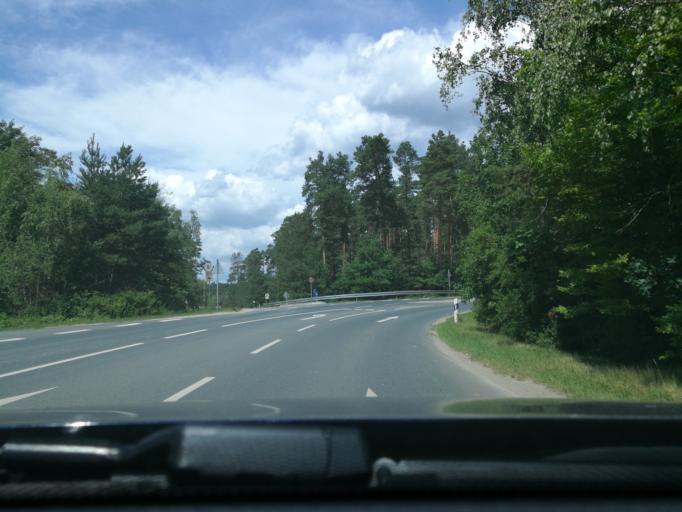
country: DE
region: Bavaria
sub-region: Regierungsbezirk Mittelfranken
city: Feucht
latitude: 49.3620
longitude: 11.2059
